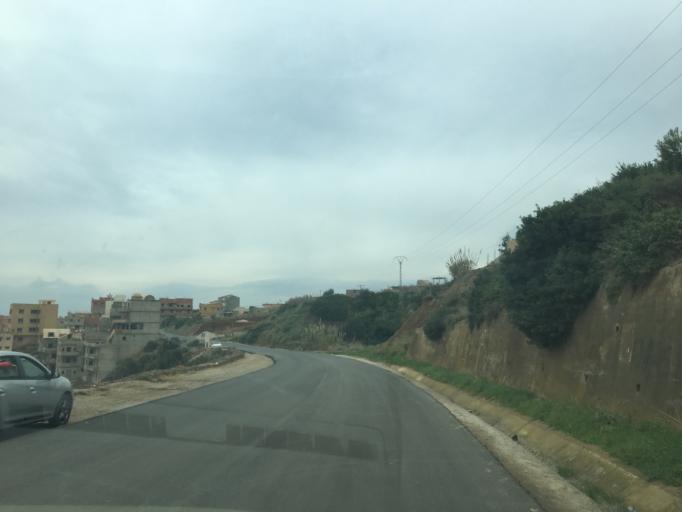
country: DZ
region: Tipaza
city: Tipasa
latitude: 36.6405
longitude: 2.3431
